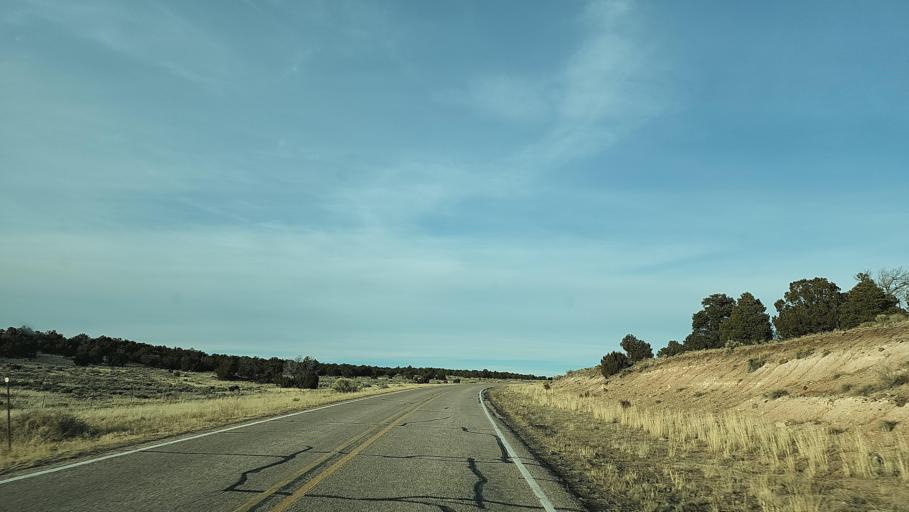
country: US
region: New Mexico
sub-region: Catron County
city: Reserve
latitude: 34.4078
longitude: -108.4364
